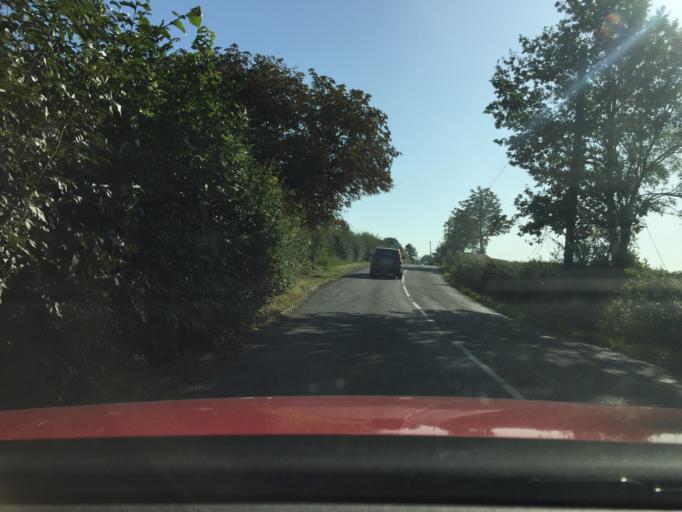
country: GB
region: England
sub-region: Leicestershire
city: Queniborough
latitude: 52.6683
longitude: -1.0258
